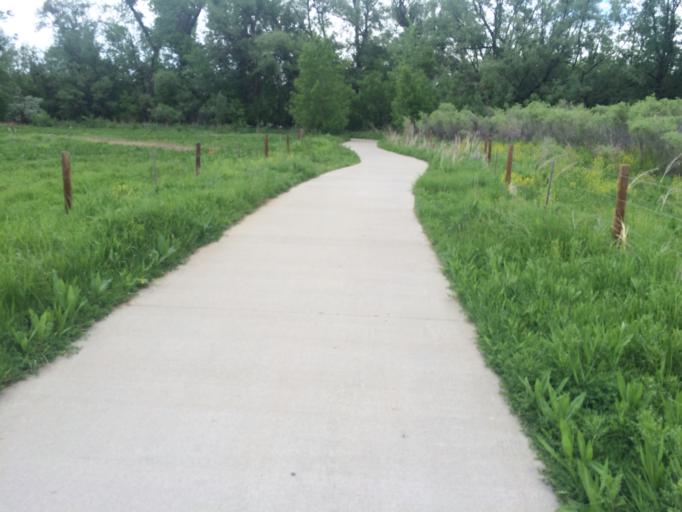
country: US
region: Colorado
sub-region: Boulder County
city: Boulder
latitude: 40.0184
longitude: -105.2350
